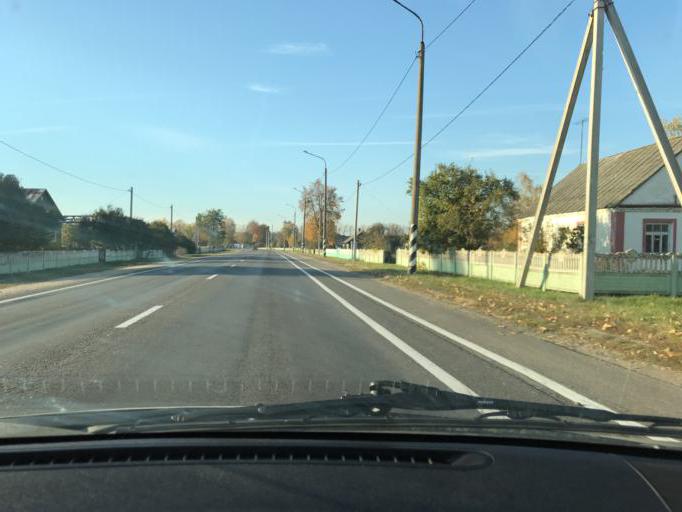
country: BY
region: Brest
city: Horad Kobryn
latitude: 52.2145
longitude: 24.5557
